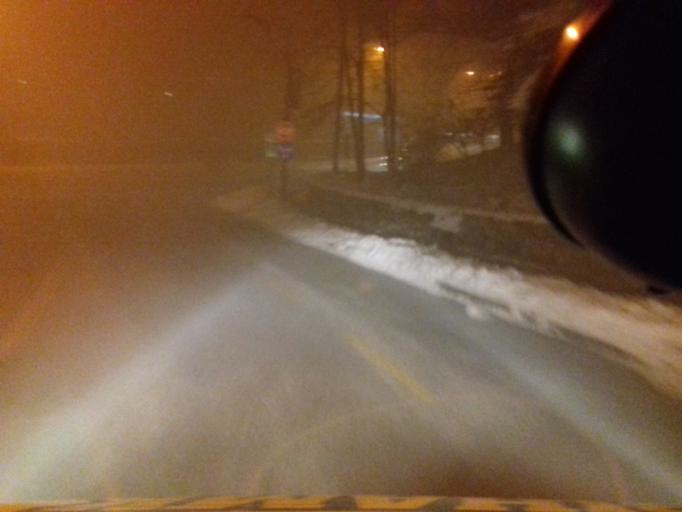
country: BA
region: Federation of Bosnia and Herzegovina
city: Kobilja Glava
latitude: 43.8669
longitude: 18.4167
